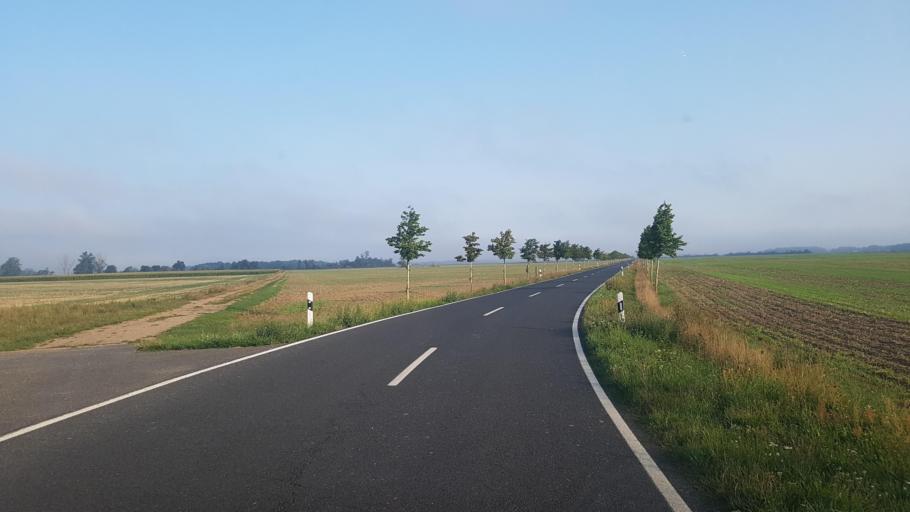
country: DE
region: Saxony-Anhalt
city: Pretzsch
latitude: 51.7135
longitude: 12.8689
